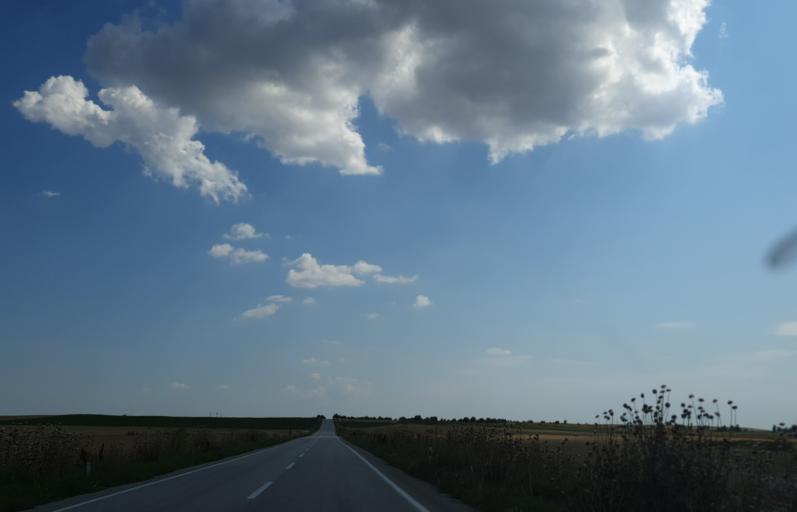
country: TR
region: Kirklareli
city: Buyukkaristiran
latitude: 41.3895
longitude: 27.5714
